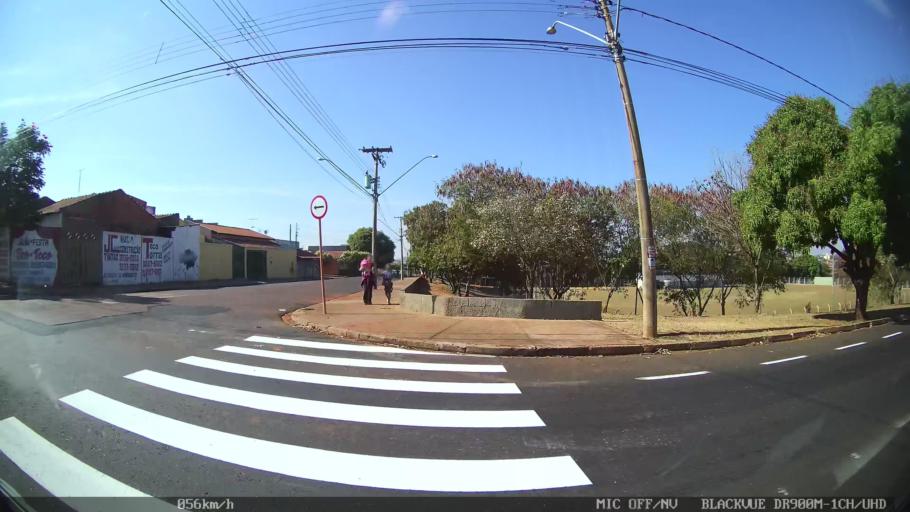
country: BR
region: Sao Paulo
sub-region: Sao Jose Do Rio Preto
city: Sao Jose do Rio Preto
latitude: -20.7874
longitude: -49.4104
